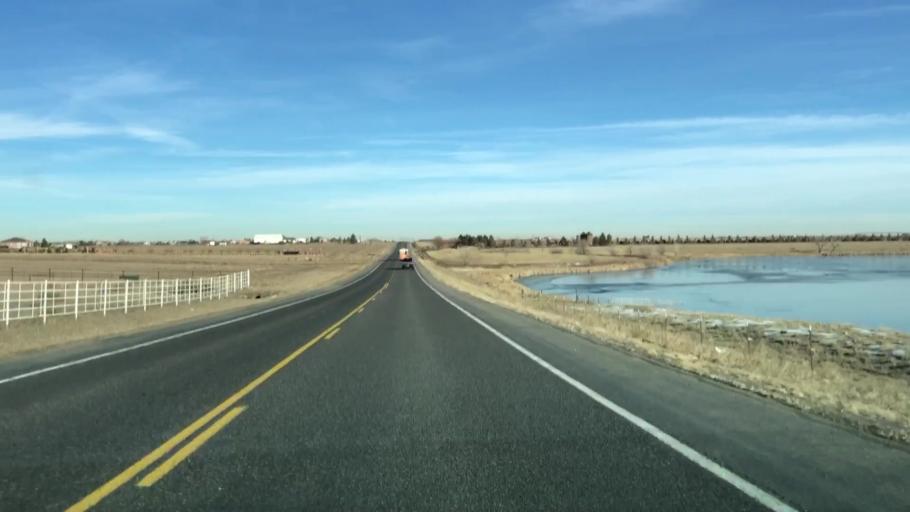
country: US
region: Colorado
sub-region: Weld County
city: Windsor
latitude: 40.4236
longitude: -104.9444
